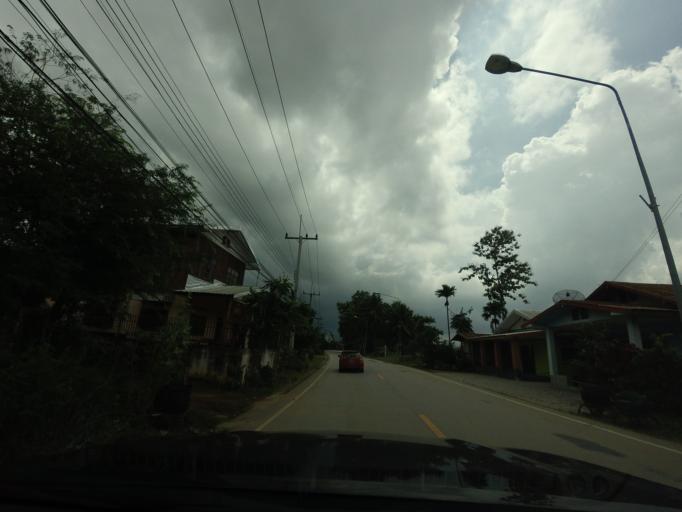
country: LA
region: Vientiane
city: Muang Sanakham
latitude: 18.0020
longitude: 101.7561
